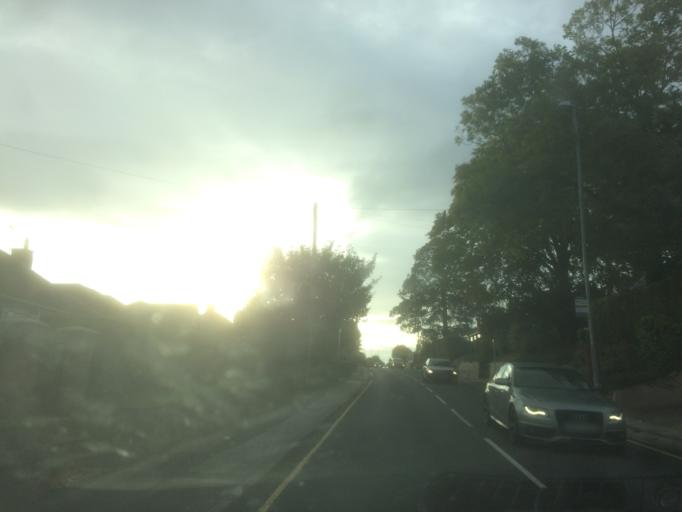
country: GB
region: England
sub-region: City and Borough of Wakefield
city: Pontefract
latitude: 53.7181
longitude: -1.3135
